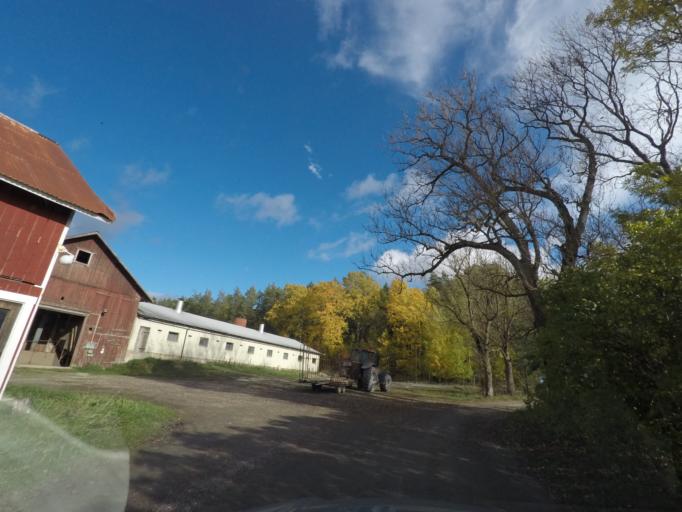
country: SE
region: Vaestmanland
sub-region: Kungsors Kommun
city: Kungsoer
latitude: 59.3386
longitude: 16.2008
